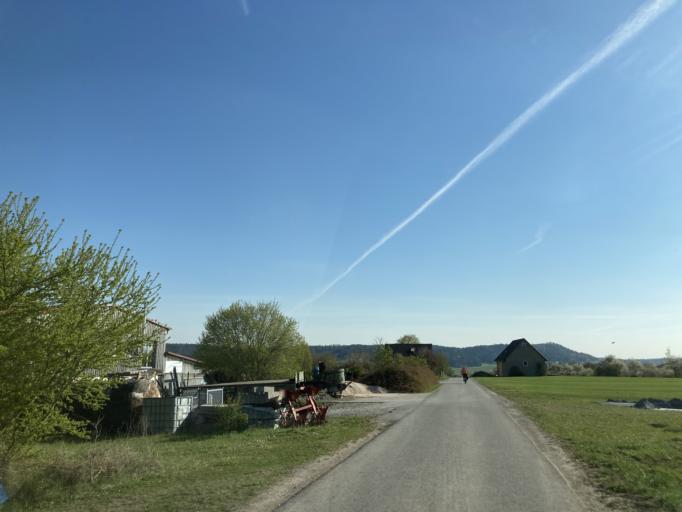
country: DE
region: Baden-Wuerttemberg
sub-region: Tuebingen Region
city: Rottenburg
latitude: 48.5415
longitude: 8.9529
